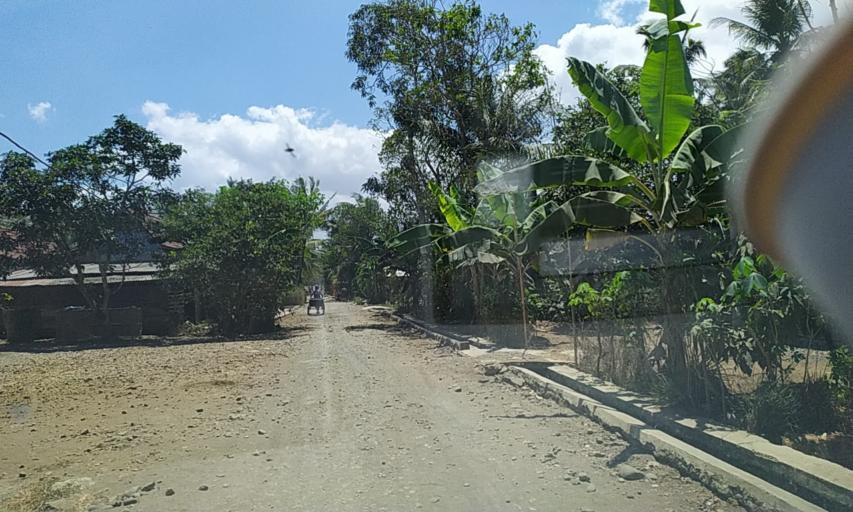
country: ID
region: Central Java
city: Mernek
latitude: -7.6267
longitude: 109.1755
